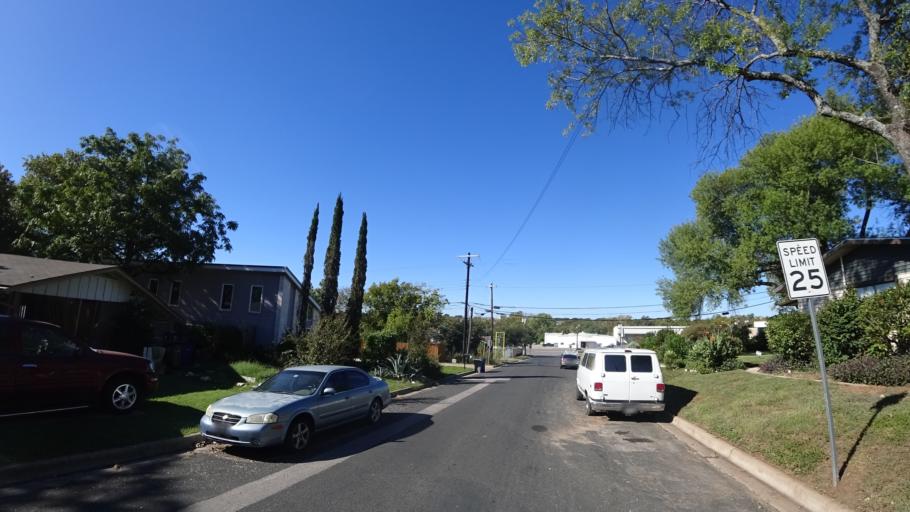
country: US
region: Texas
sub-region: Travis County
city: Austin
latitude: 30.2879
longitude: -97.7056
